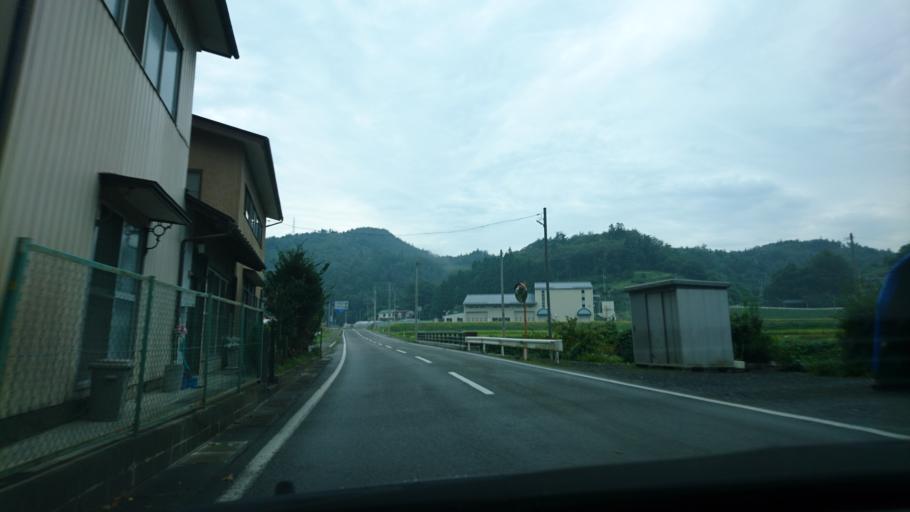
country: JP
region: Iwate
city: Ichinoseki
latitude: 39.0070
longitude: 141.2611
